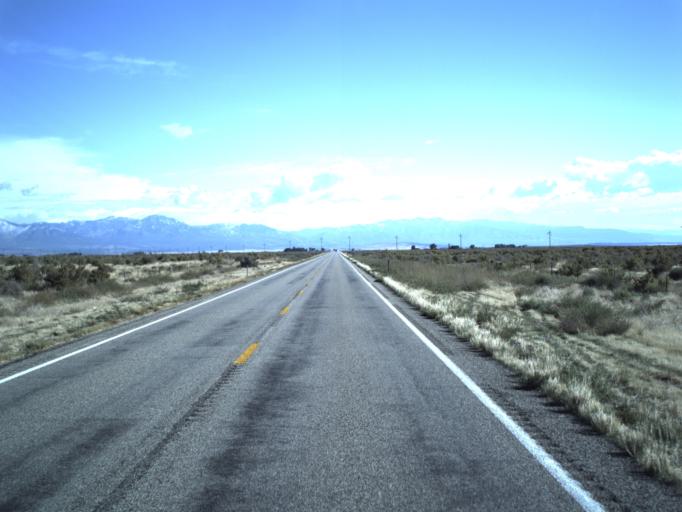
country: US
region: Utah
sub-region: Millard County
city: Delta
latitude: 39.2329
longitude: -112.4284
